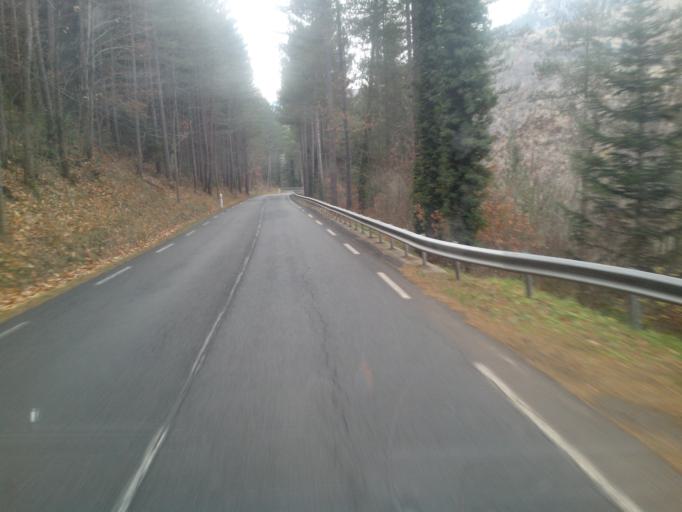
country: FR
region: Languedoc-Roussillon
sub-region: Departement de la Lozere
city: Florac
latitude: 44.3820
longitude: 3.5581
